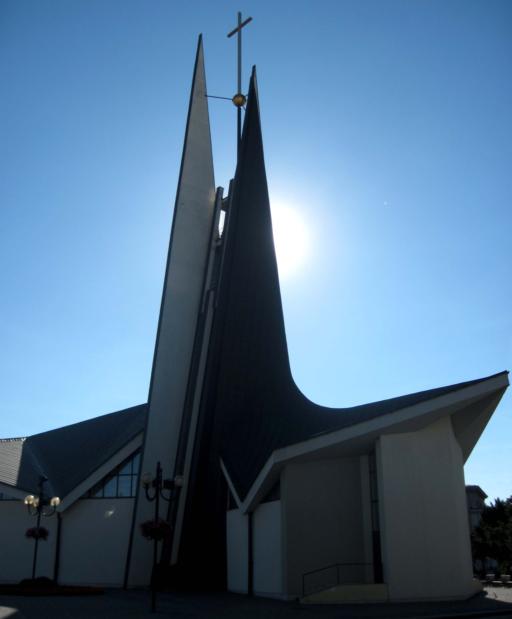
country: CZ
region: South Moravian
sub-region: Okres Breclav
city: Breclav
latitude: 48.7597
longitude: 16.8814
